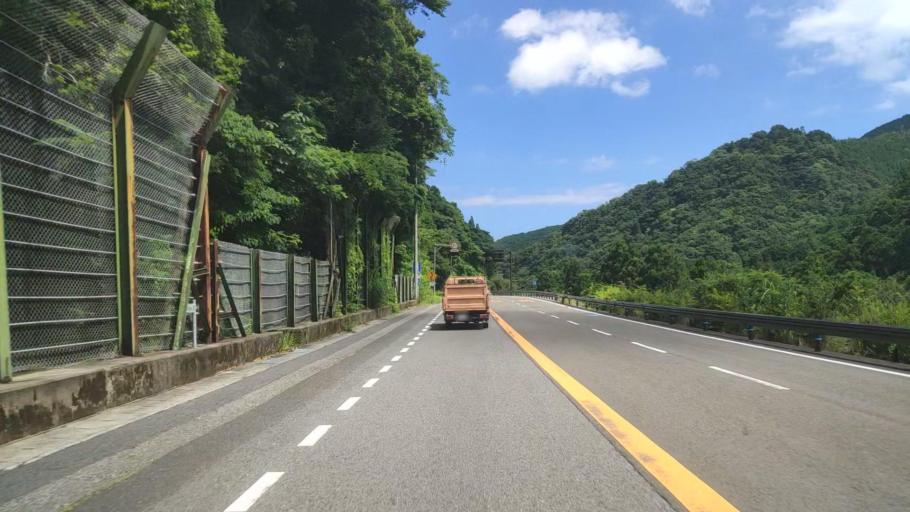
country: JP
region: Mie
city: Owase
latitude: 33.9234
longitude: 136.0947
